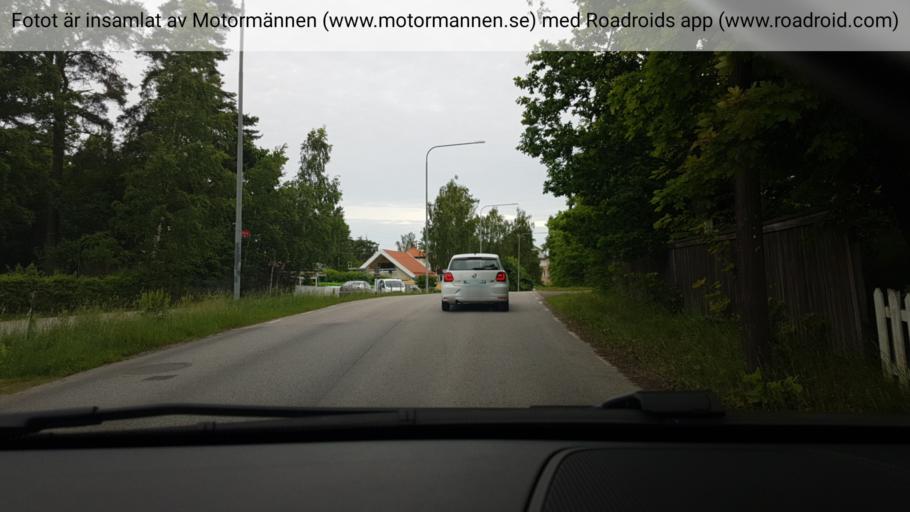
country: SE
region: Stockholm
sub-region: Huddinge Kommun
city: Huddinge
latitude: 59.2377
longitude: 17.9949
